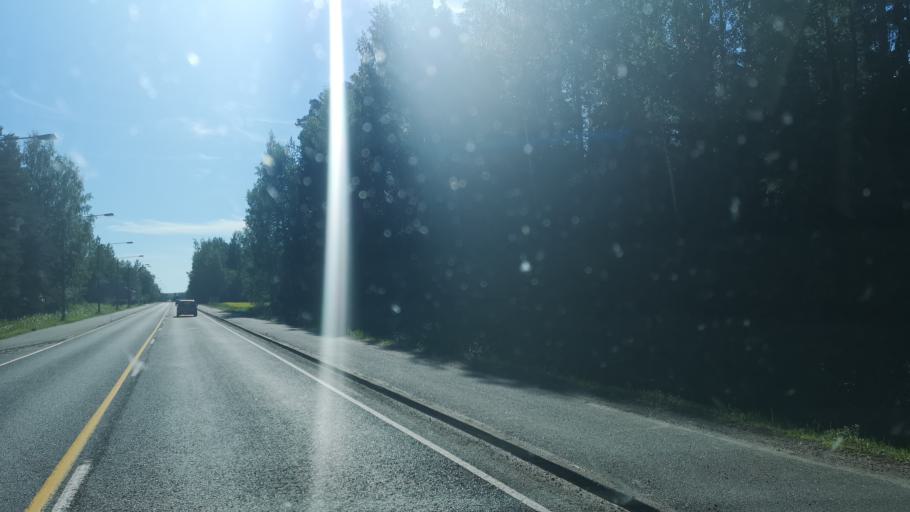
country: FI
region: Southern Ostrobothnia
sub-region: Seinaejoki
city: Lapua
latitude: 62.9694
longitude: 23.0543
